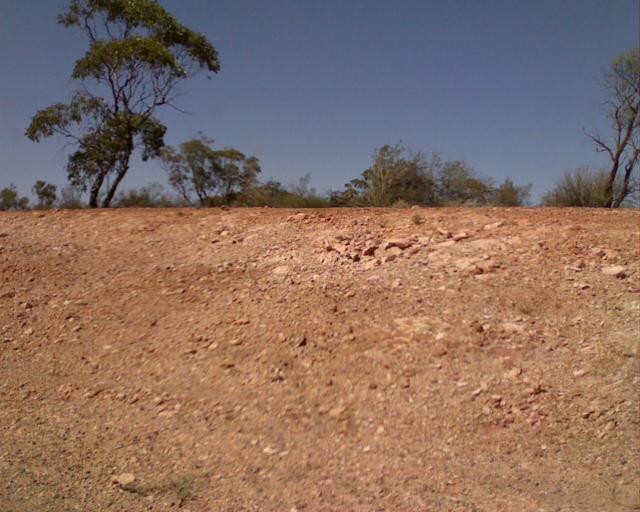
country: AU
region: Western Australia
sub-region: Kalgoorlie/Boulder
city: Boulder
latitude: -30.8411
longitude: 121.3882
